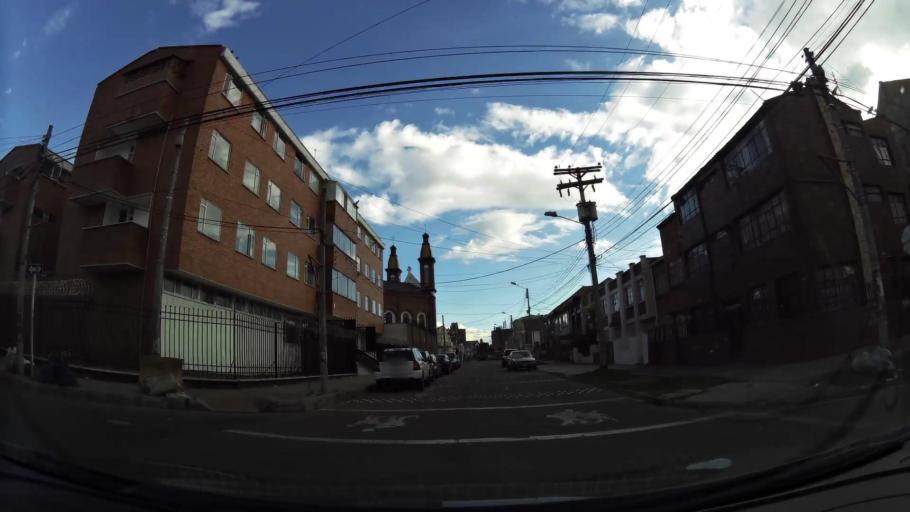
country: CO
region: Bogota D.C.
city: Bogota
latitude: 4.6522
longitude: -74.0681
